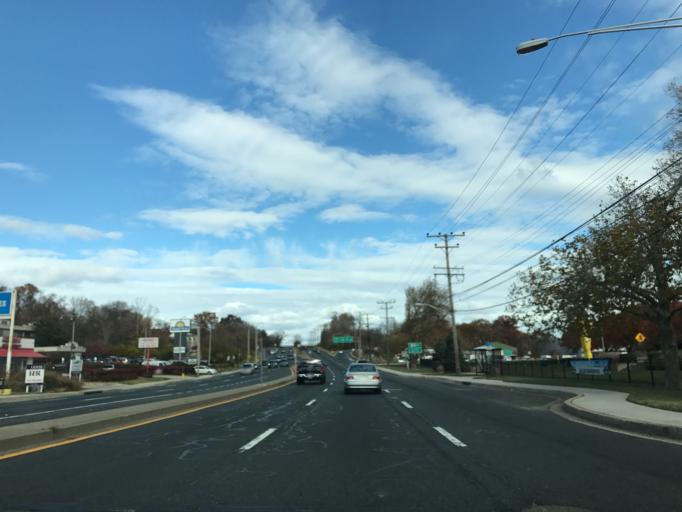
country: US
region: Maryland
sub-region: Anne Arundel County
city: Ferndale
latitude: 39.1968
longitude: -76.6132
